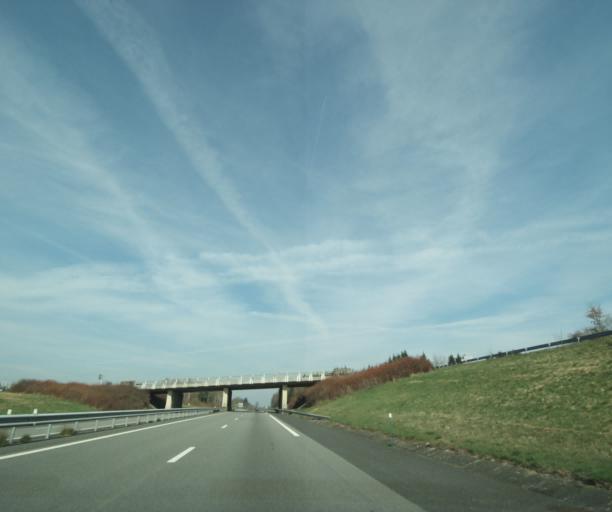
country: FR
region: Limousin
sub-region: Departement de la Correze
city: Saint-Mexant
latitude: 45.3187
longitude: 1.5739
